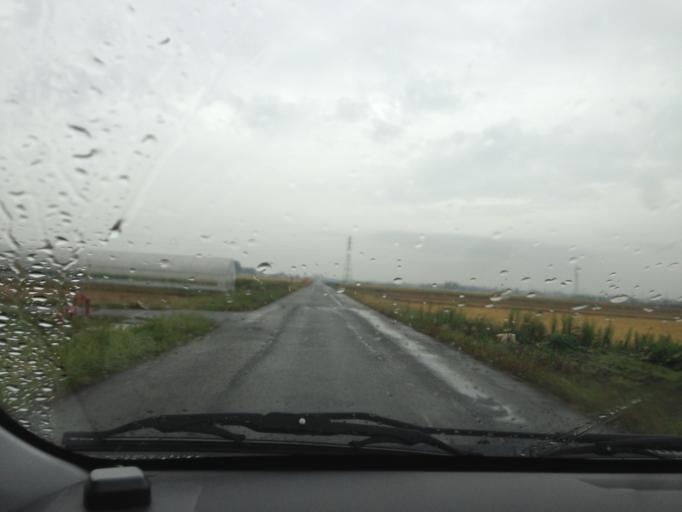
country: JP
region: Fukushima
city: Kitakata
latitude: 37.5044
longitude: 139.9007
